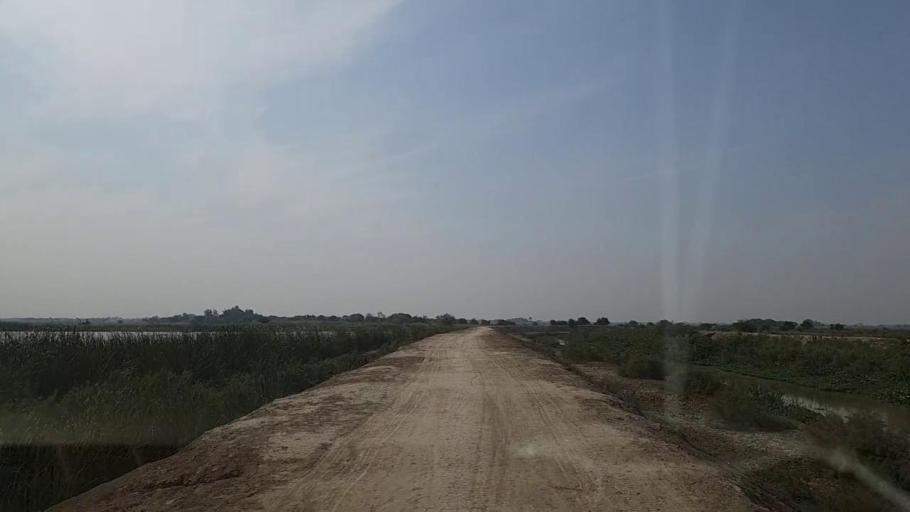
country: PK
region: Sindh
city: Mirpur Batoro
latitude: 24.6572
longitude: 68.2471
